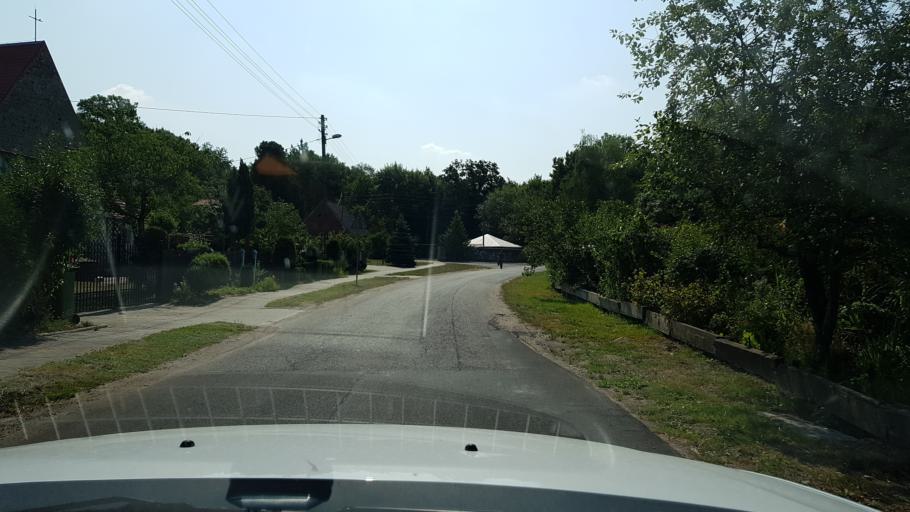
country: PL
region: West Pomeranian Voivodeship
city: Trzcinsko Zdroj
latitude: 52.9215
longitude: 14.5348
